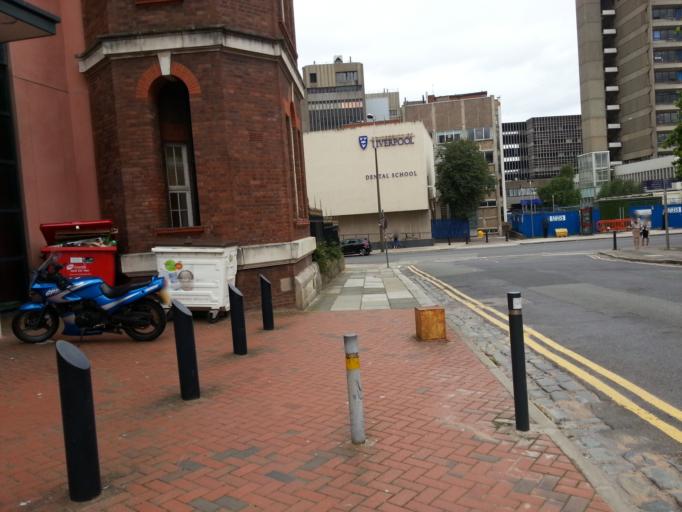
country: GB
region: England
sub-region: Liverpool
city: Liverpool
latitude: 53.4082
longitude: -2.9663
